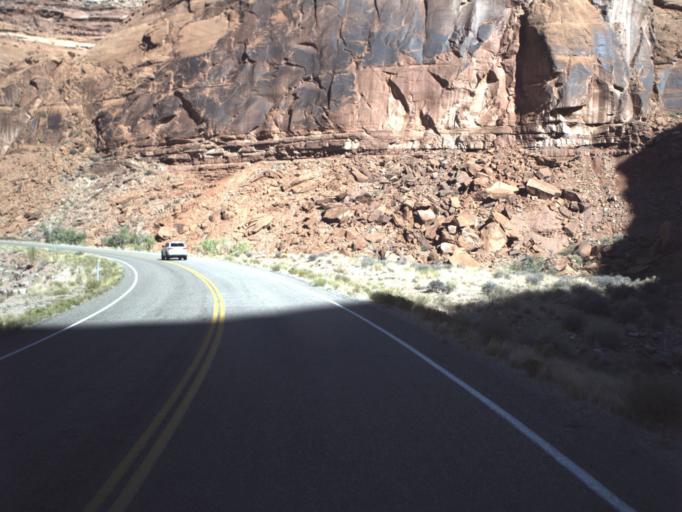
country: US
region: Utah
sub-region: San Juan County
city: Blanding
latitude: 37.9585
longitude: -110.4807
